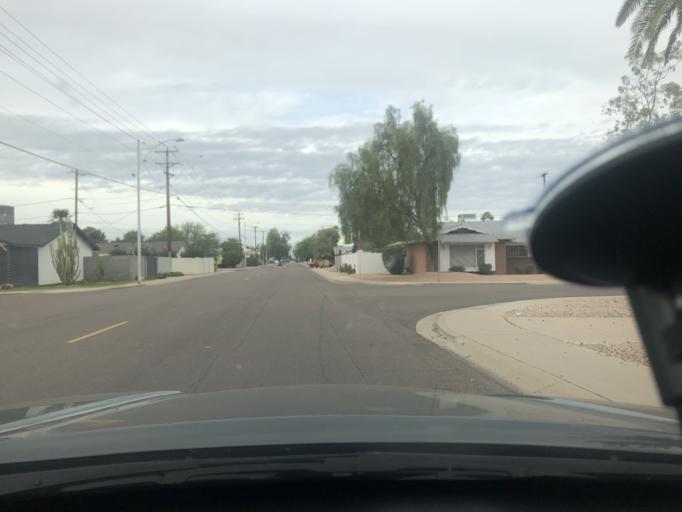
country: US
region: Arizona
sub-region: Maricopa County
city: Scottsdale
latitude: 33.4924
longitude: -111.9046
